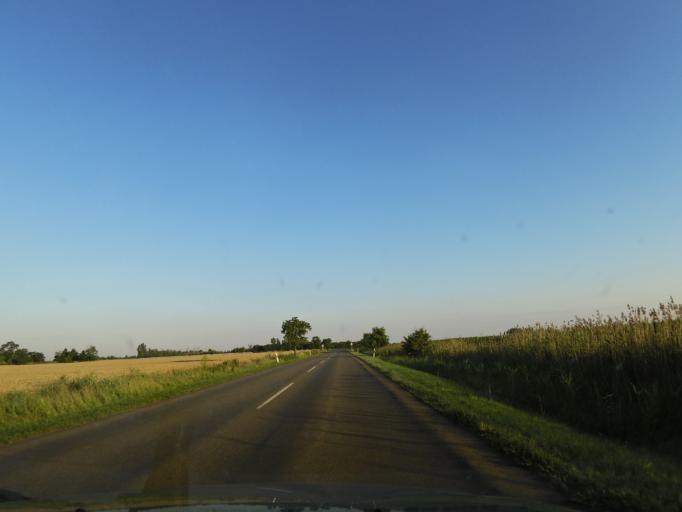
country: HU
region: Csongrad
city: Szentes
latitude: 46.5863
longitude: 20.2998
